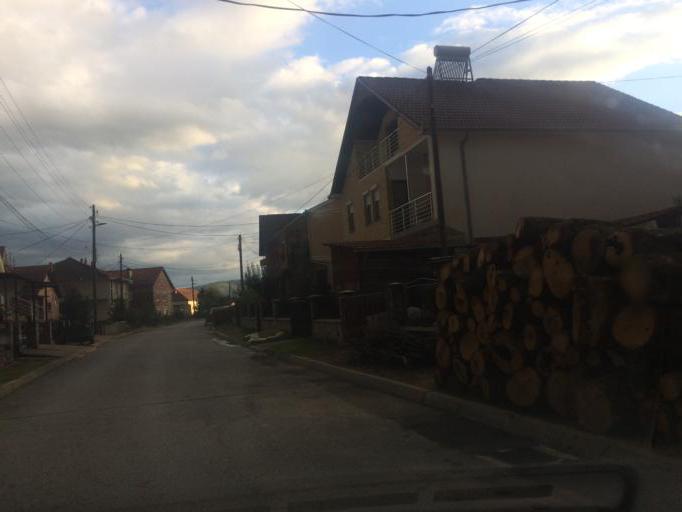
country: MK
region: Makedonska Kamenica
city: Makedonska Kamenica
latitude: 42.0262
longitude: 22.5856
